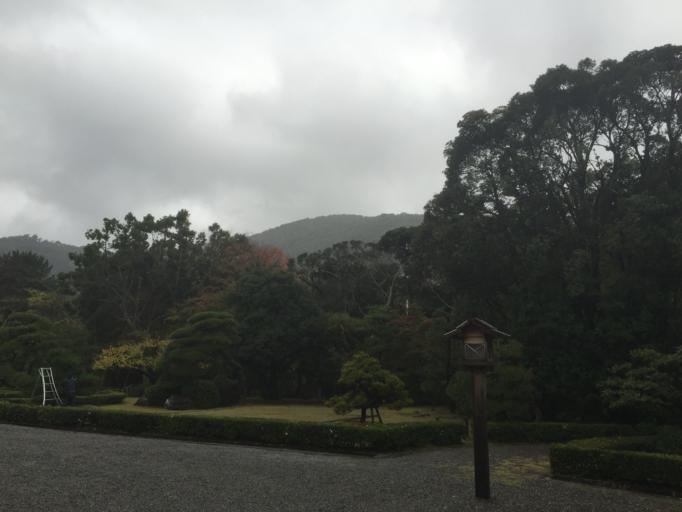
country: JP
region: Mie
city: Ise
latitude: 34.4579
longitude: 136.7234
